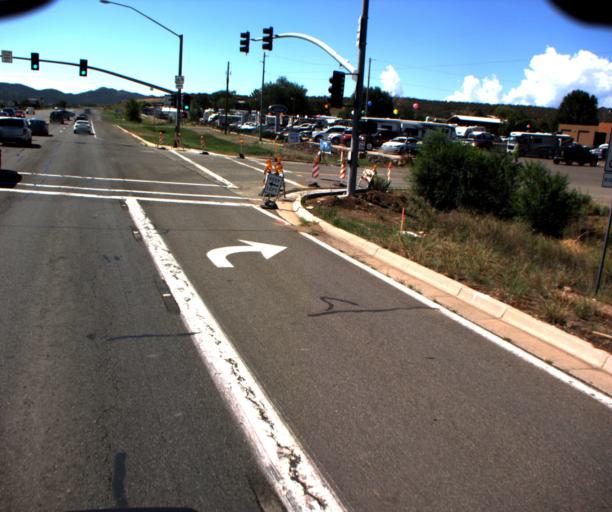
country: US
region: Arizona
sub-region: Yavapai County
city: Dewey-Humboldt
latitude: 34.5301
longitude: -112.2424
